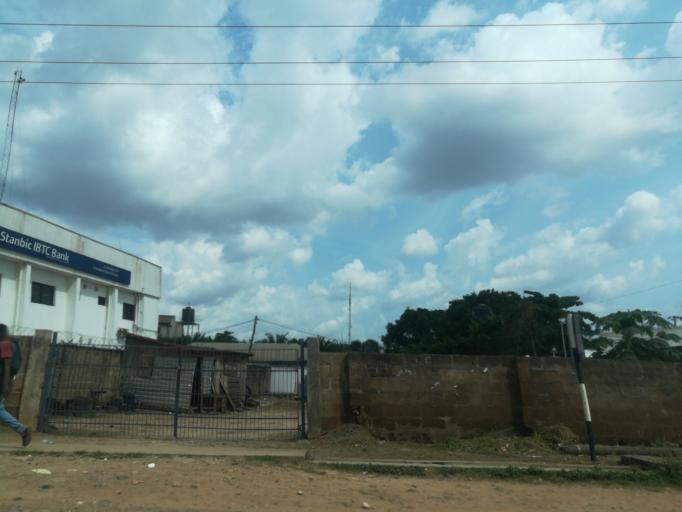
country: NG
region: Oyo
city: Ibadan
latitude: 7.3990
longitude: 3.9093
